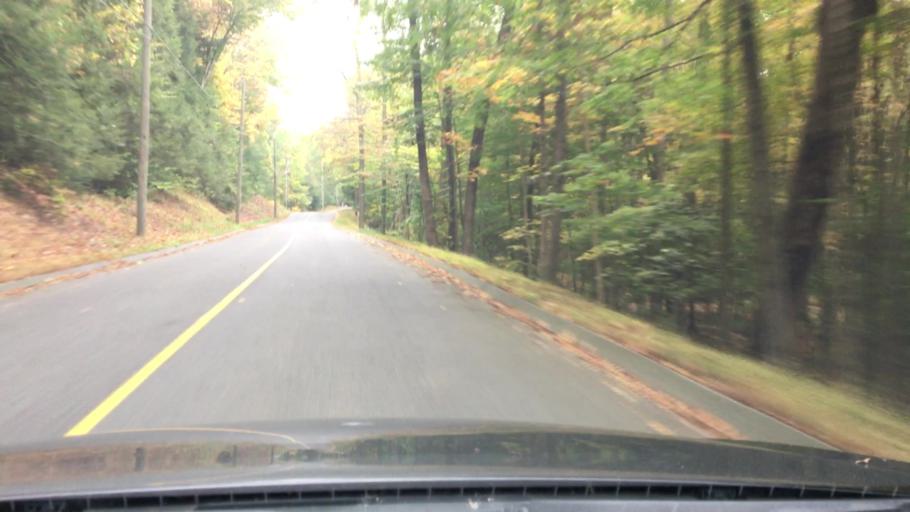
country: US
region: Connecticut
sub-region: New Haven County
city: Heritage Village
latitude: 41.5046
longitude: -73.2676
